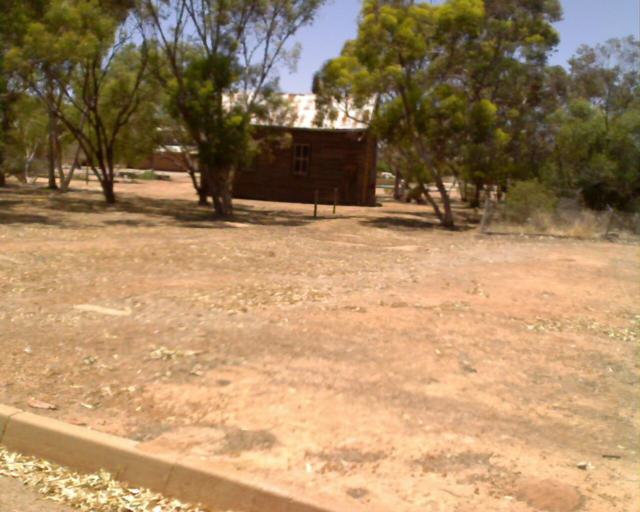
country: AU
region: Western Australia
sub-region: Wongan-Ballidu
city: Wongan Hills
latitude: -30.8276
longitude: 117.4807
